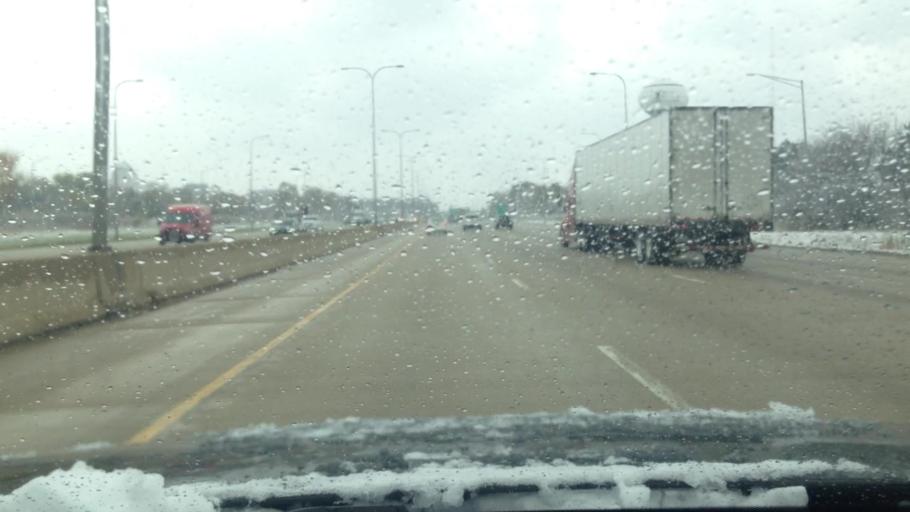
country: US
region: Illinois
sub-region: DuPage County
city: Itasca
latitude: 42.0012
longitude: -88.0259
